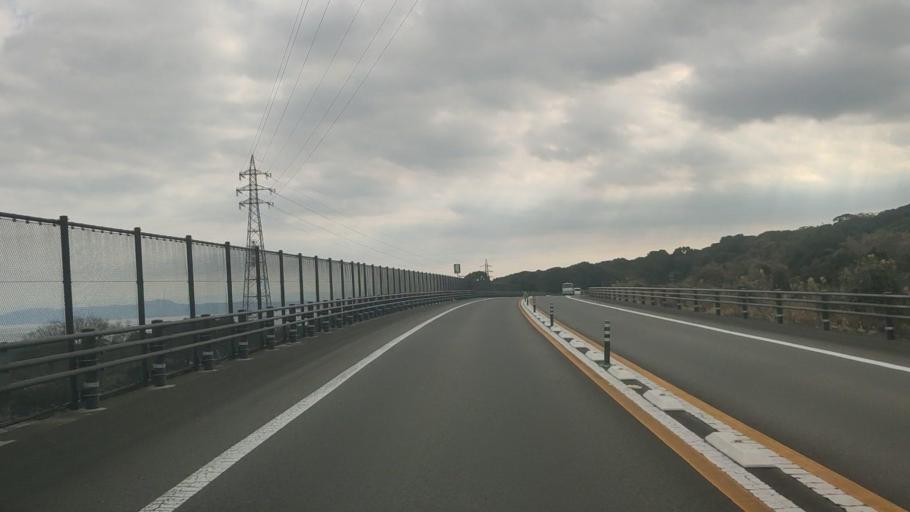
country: JP
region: Nagasaki
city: Shimabara
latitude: 32.7825
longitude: 130.3539
